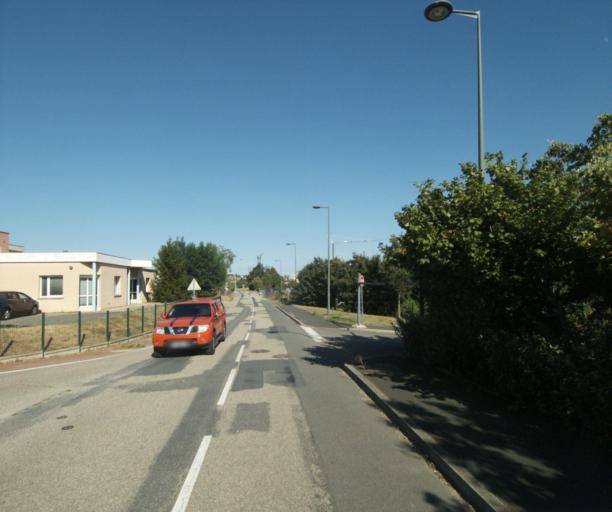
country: FR
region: Rhone-Alpes
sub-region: Departement du Rhone
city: Lentilly
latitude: 45.8169
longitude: 4.6831
